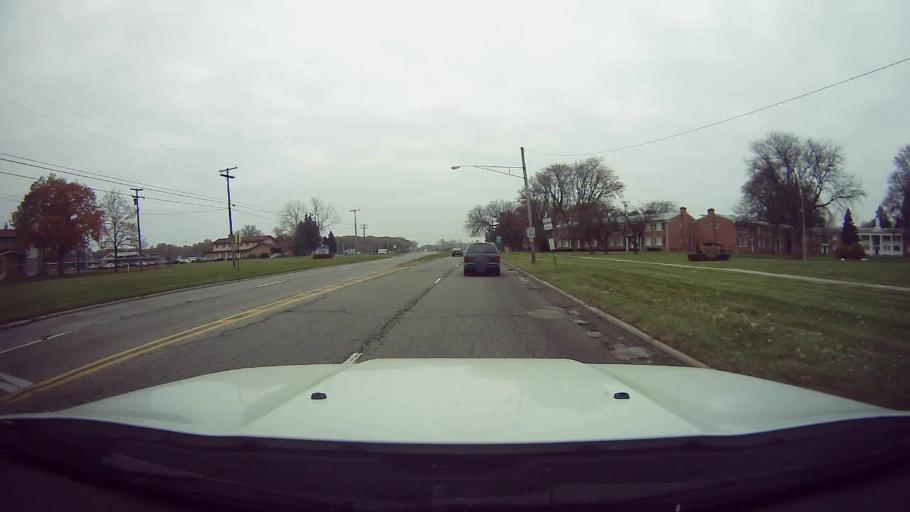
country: US
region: Michigan
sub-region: Wayne County
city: Dearborn Heights
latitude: 42.3322
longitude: -83.2350
